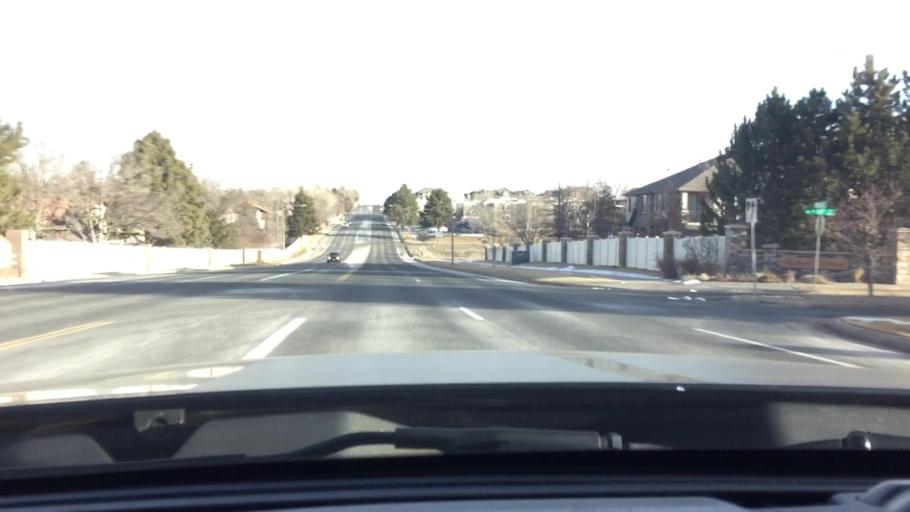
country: US
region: Colorado
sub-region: Adams County
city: Northglenn
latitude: 39.9024
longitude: -105.0061
